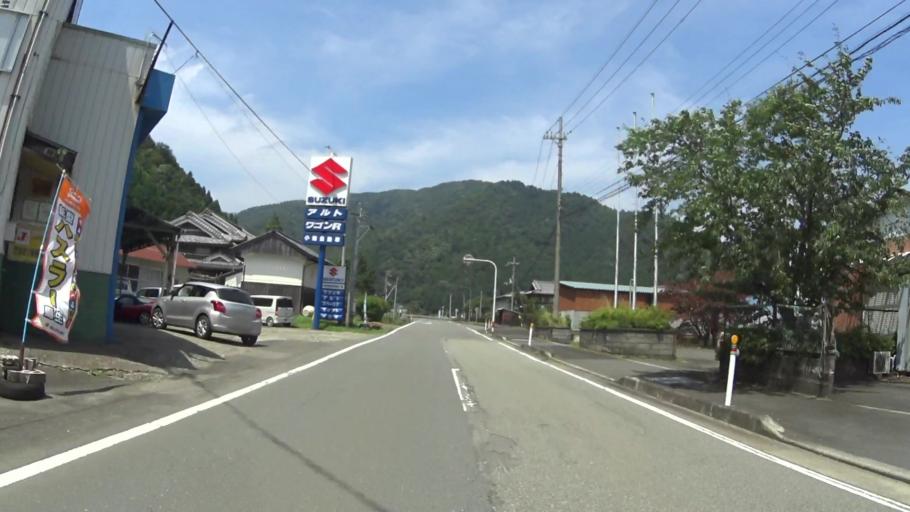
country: JP
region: Kyoto
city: Maizuru
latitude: 35.3178
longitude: 135.5567
